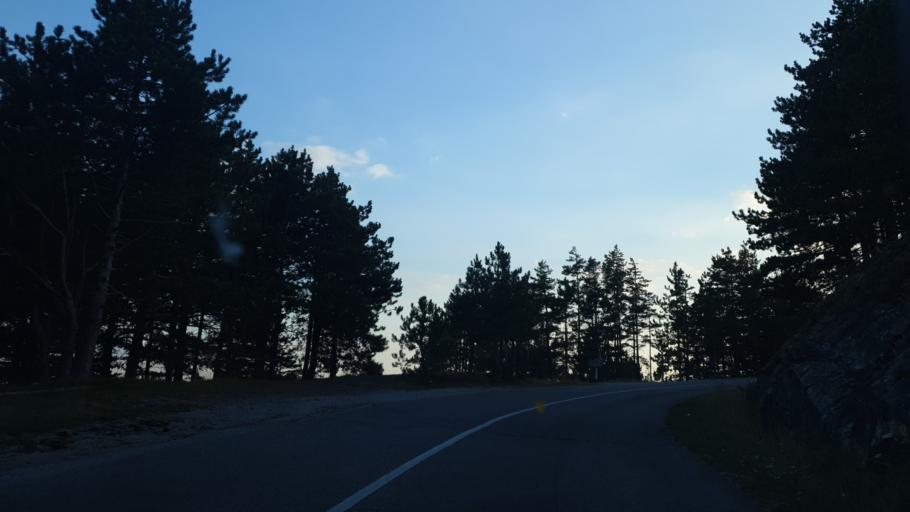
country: RS
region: Central Serbia
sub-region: Zlatiborski Okrug
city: Kosjeric
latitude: 44.0875
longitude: 19.9983
